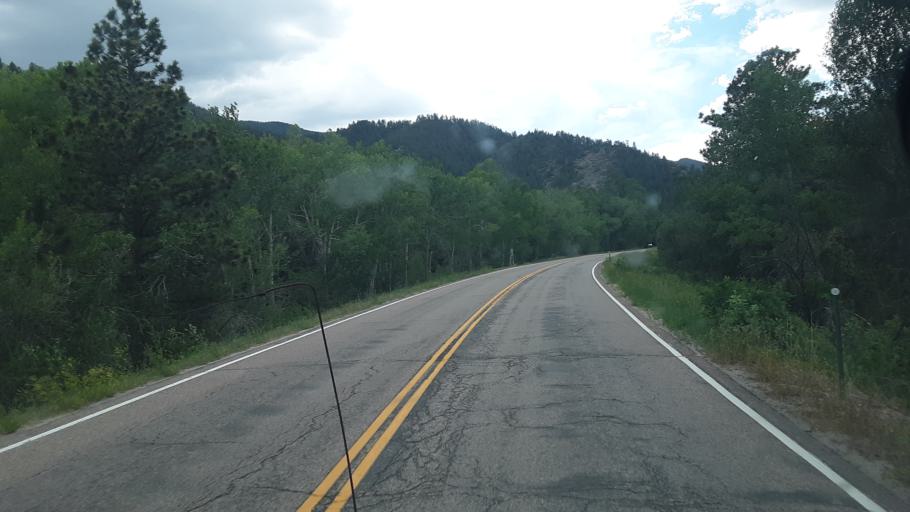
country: US
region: Colorado
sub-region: Fremont County
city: Florence
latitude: 38.1763
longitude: -105.1244
